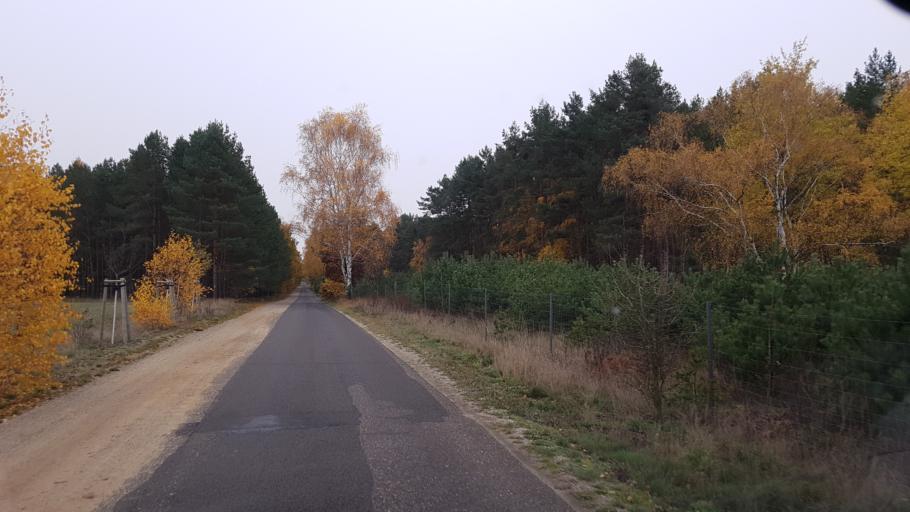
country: DE
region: Brandenburg
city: Crinitz
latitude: 51.7193
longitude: 13.7775
